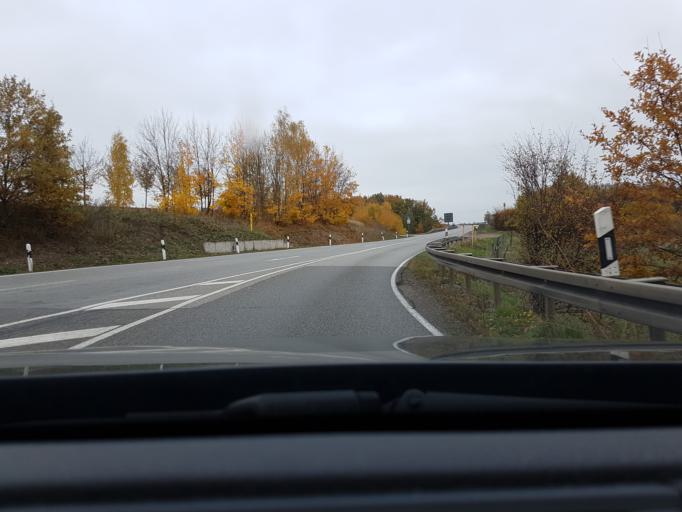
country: DE
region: Saxony
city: Hilbersdorf
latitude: 50.9101
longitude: 12.9772
